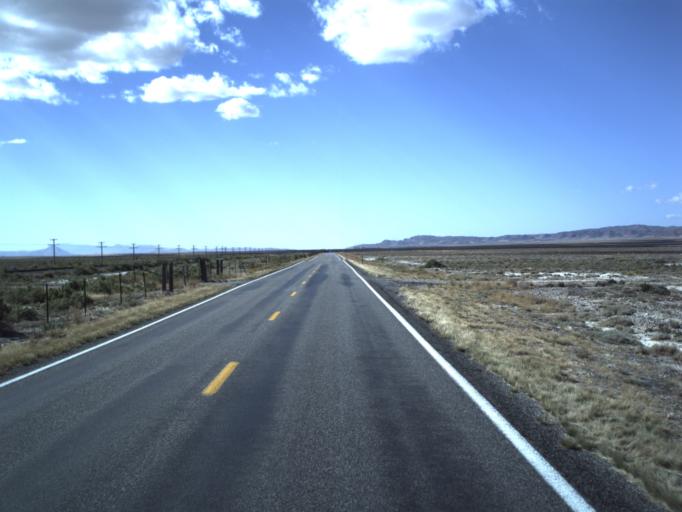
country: US
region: Utah
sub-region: Millard County
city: Delta
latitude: 39.0457
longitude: -112.7693
